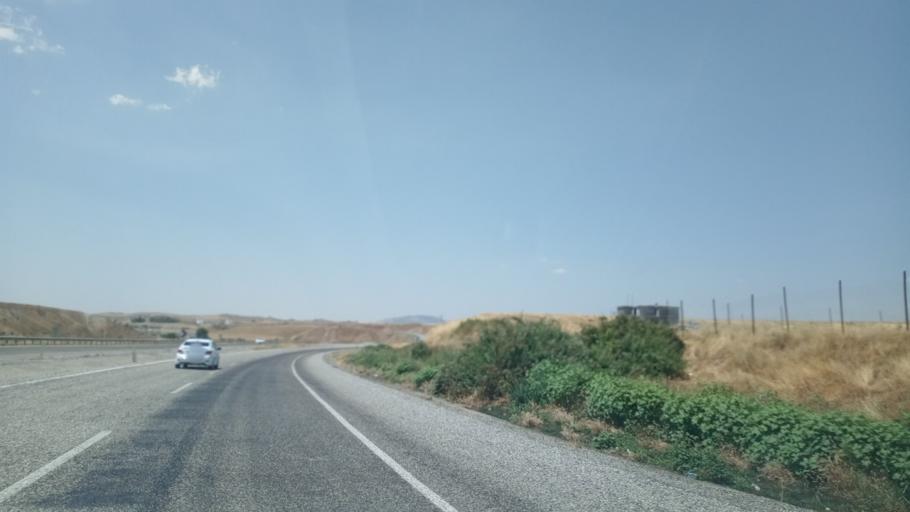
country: TR
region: Batman
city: Bekirhan
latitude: 38.1512
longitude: 41.3160
